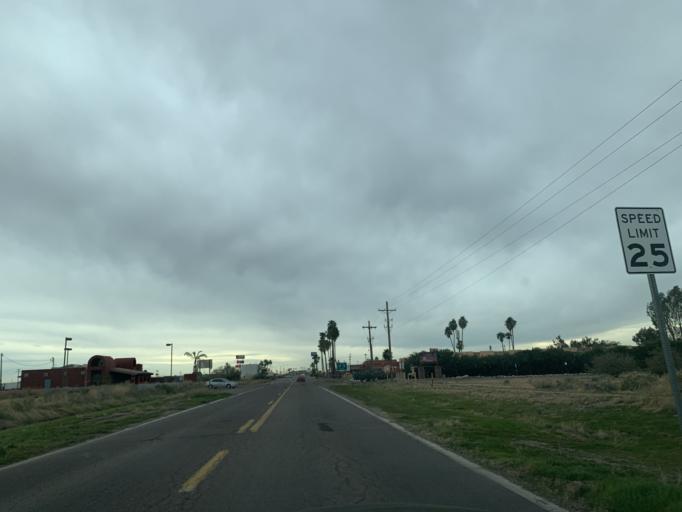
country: US
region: Arizona
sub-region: Pinal County
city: Arizona City
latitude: 32.8162
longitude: -111.6711
